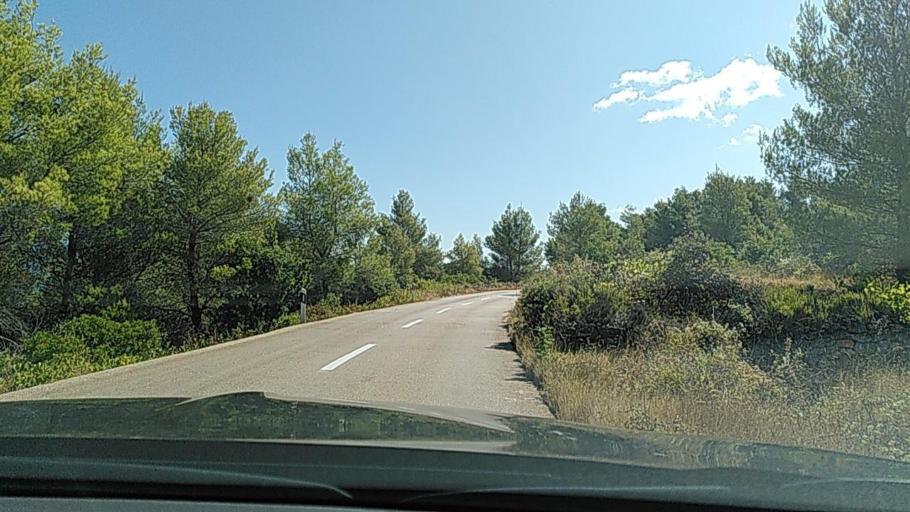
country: HR
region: Splitsko-Dalmatinska
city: Jelsa
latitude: 43.1446
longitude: 16.8050
